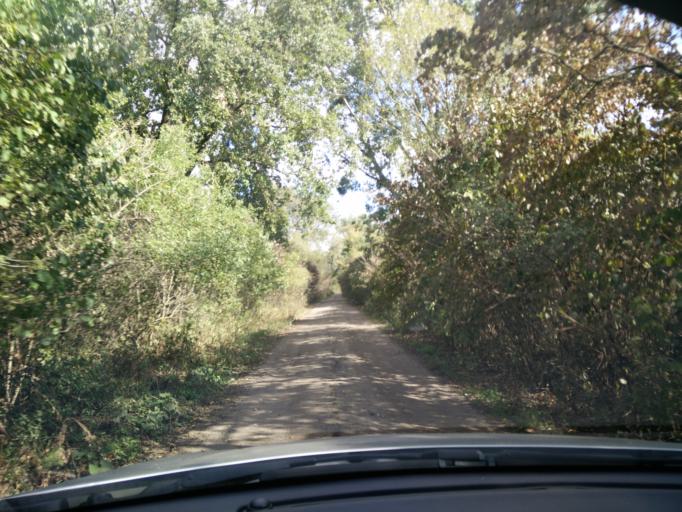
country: PL
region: Greater Poland Voivodeship
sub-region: Powiat sredzki
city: Sroda Wielkopolska
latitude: 52.2810
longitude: 17.2566
